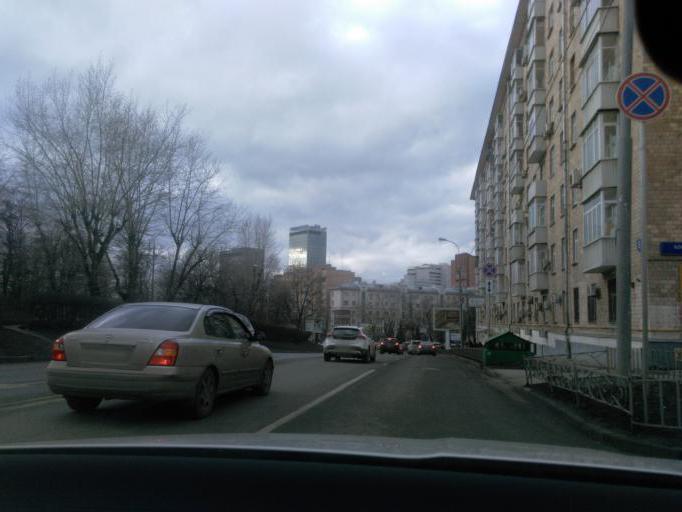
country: RU
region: Moskovskaya
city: Dorogomilovo
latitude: 55.7607
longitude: 37.5587
